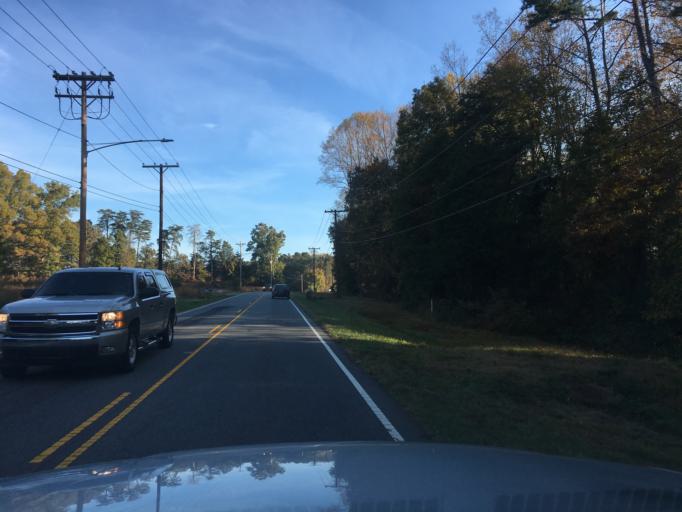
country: US
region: North Carolina
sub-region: Catawba County
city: Newton
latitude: 35.6693
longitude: -81.2475
